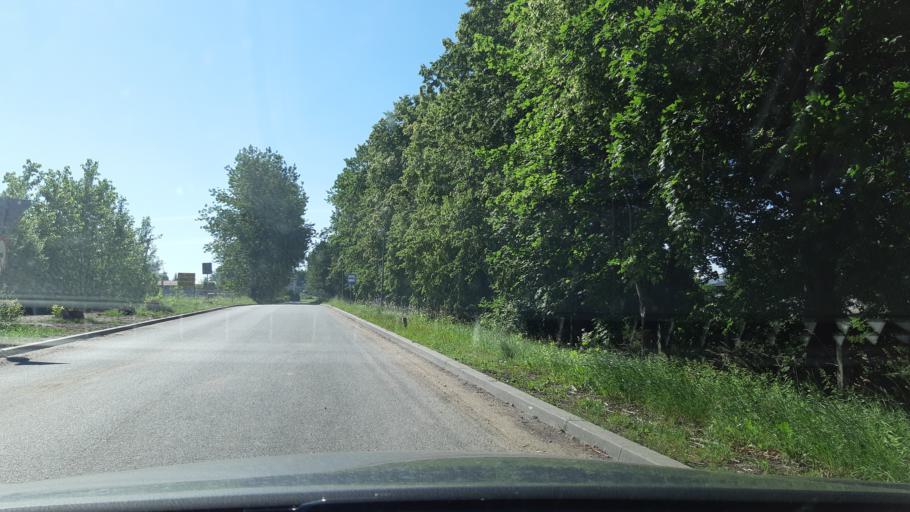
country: PL
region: Warmian-Masurian Voivodeship
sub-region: Powiat mragowski
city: Mragowo
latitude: 53.8532
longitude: 21.2921
